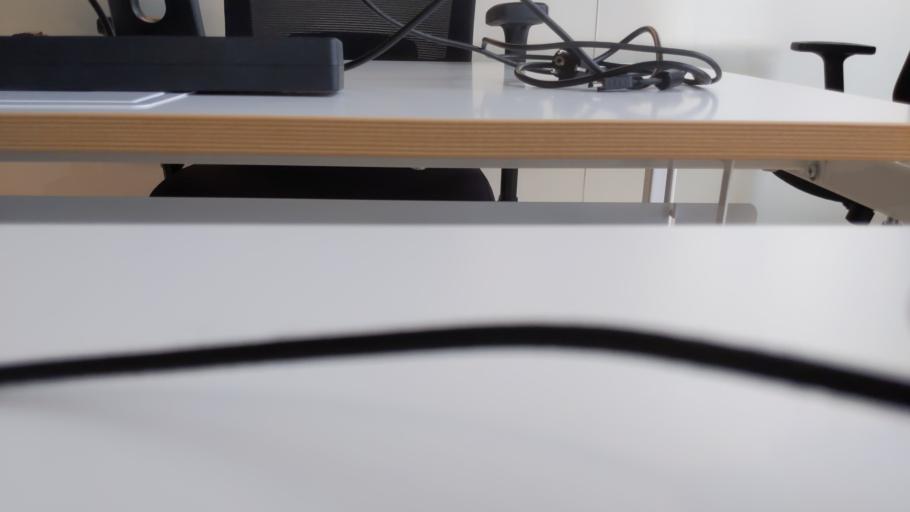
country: RU
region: Moskovskaya
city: Shevlyakovo
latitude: 56.4224
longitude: 36.9965
